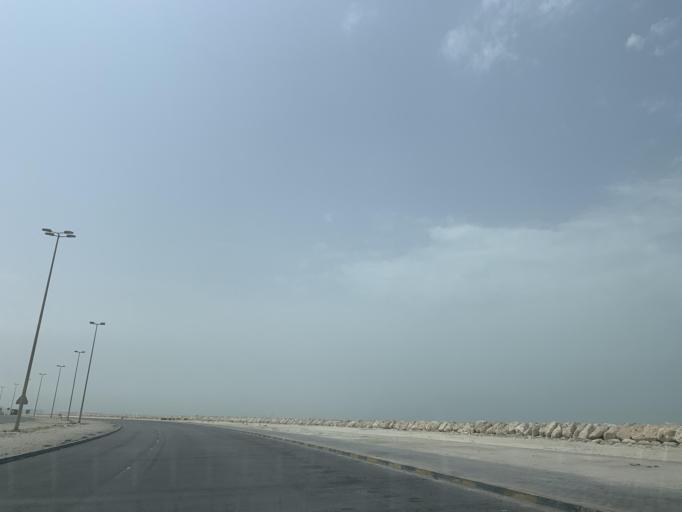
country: BH
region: Muharraq
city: Al Hadd
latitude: 26.2251
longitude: 50.6947
